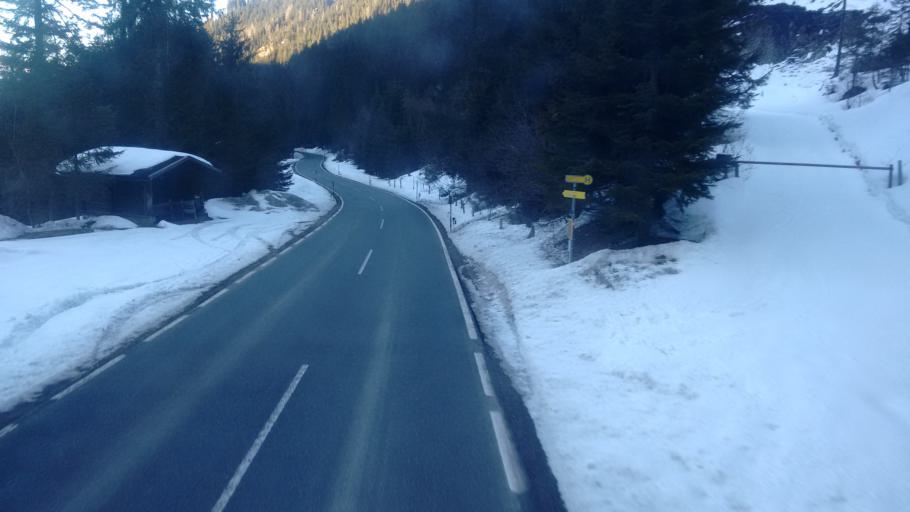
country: AT
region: Salzburg
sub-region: Politischer Bezirk Sankt Johann im Pongau
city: Radstadt
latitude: 47.3283
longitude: 13.4453
